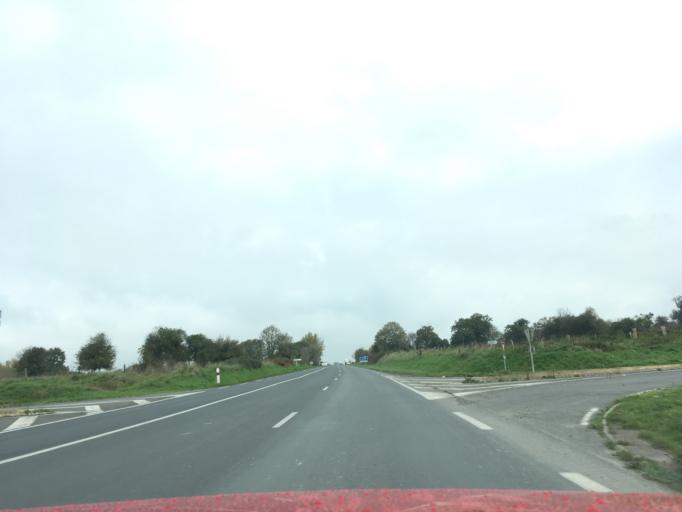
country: FR
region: Lower Normandy
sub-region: Departement de la Manche
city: Saint-Planchers
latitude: 48.8239
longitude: -1.5475
